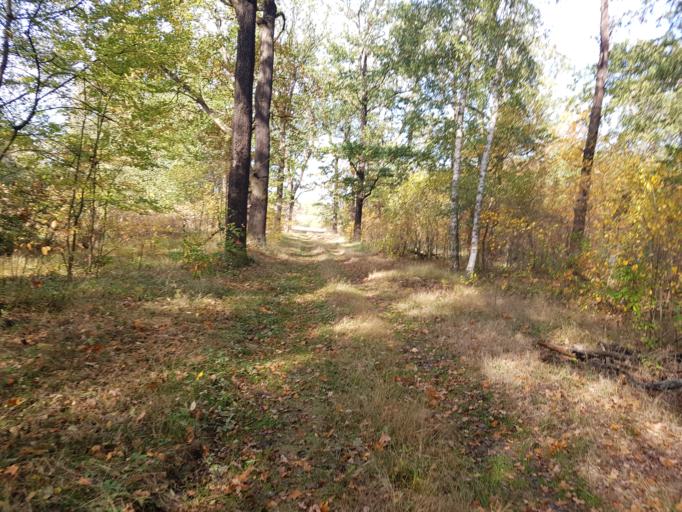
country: DE
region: Brandenburg
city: Schilda
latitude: 51.5930
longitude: 13.3356
